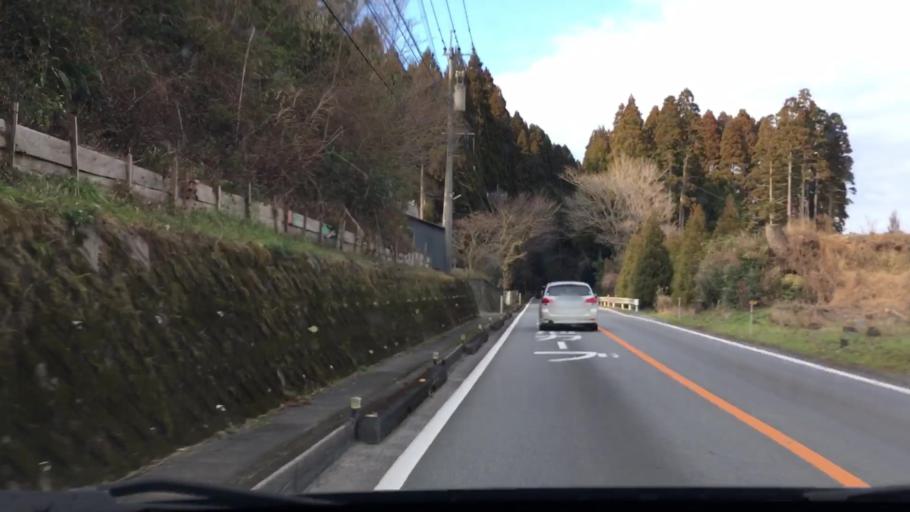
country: JP
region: Miyazaki
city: Nichinan
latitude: 31.7266
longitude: 131.3305
